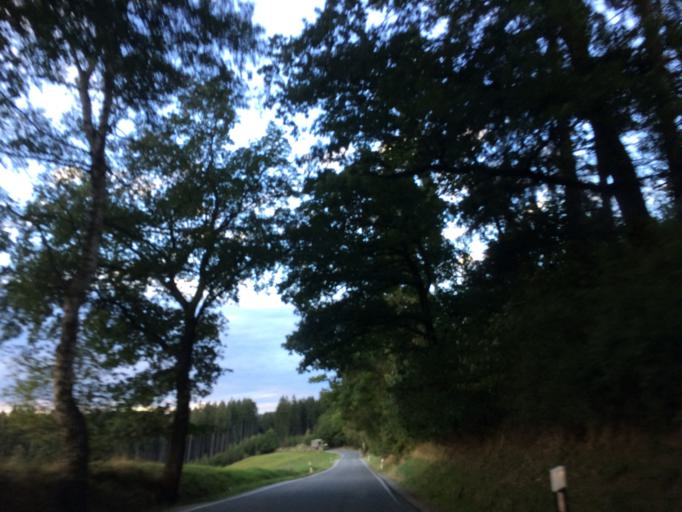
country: DE
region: Thuringia
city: Bucha
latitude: 50.6389
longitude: 11.7055
